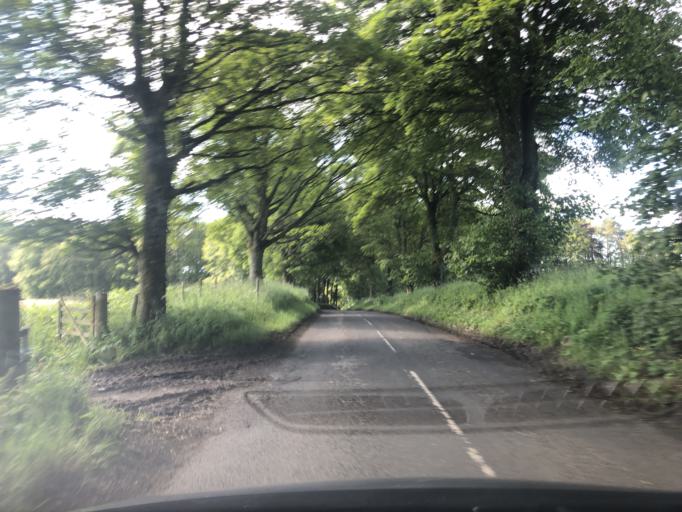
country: GB
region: Scotland
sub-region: Angus
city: Kirriemuir
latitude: 56.7318
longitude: -3.0044
